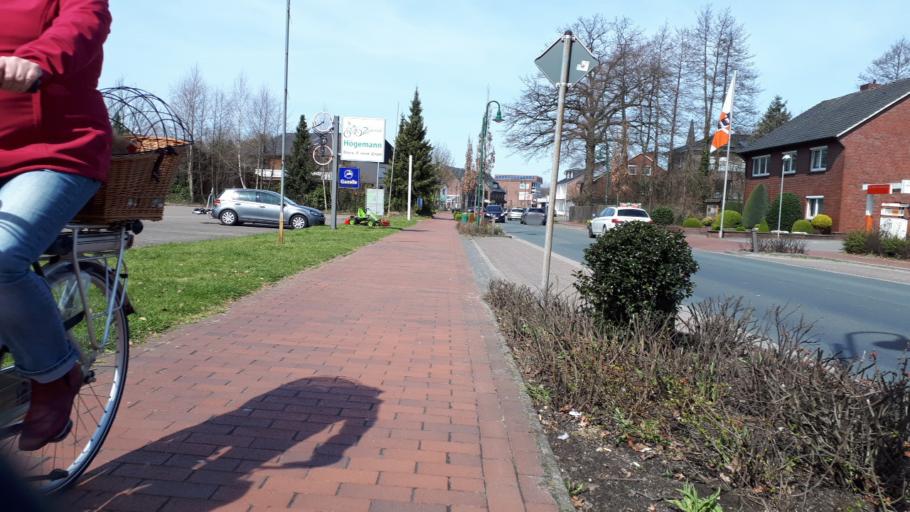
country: DE
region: Lower Saxony
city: Garrel
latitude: 52.9528
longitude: 8.0261
